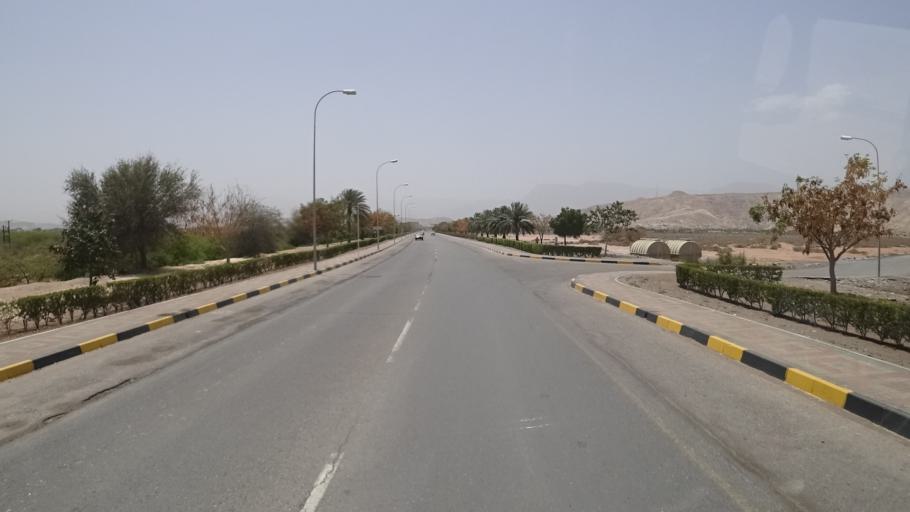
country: OM
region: Muhafazat Masqat
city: Muscat
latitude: 23.2503
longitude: 58.9064
